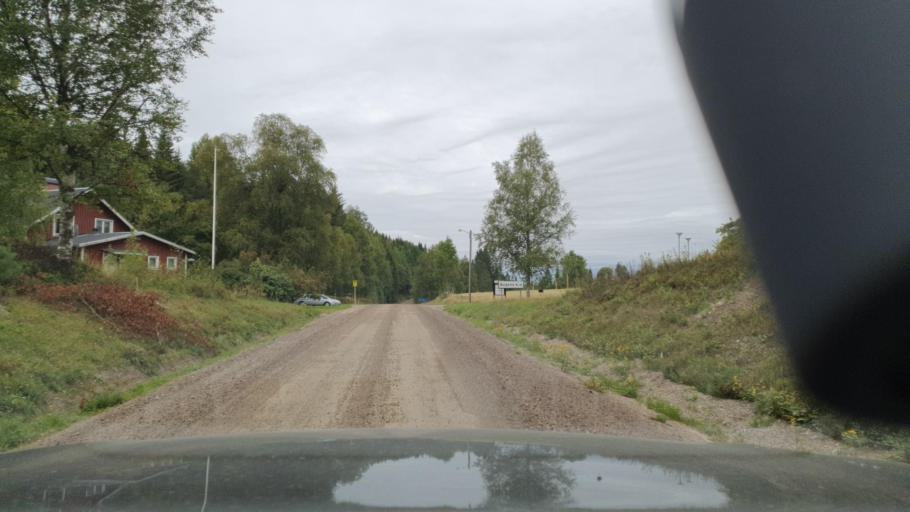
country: SE
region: Vaermland
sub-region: Eda Kommun
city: Charlottenberg
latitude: 60.0582
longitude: 12.5551
